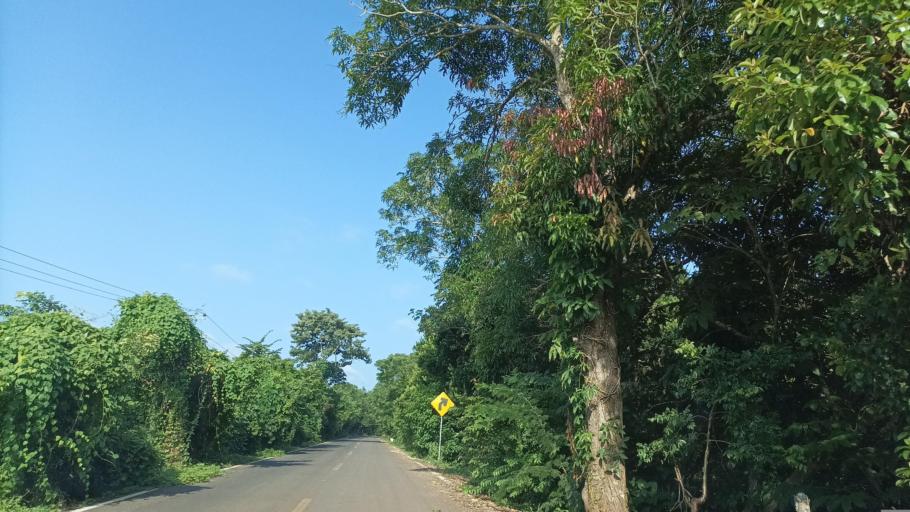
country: MX
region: Veracruz
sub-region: Chinameca
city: Chacalapa
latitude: 18.1380
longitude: -94.6494
